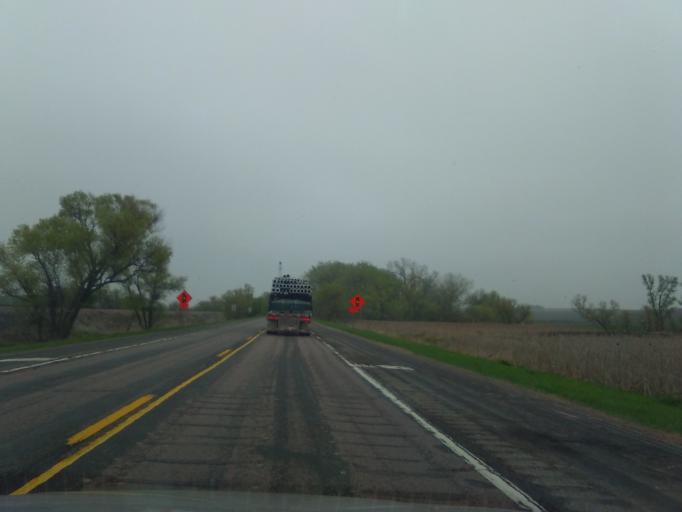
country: US
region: Nebraska
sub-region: Burt County
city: Oakland
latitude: 41.8057
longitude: -96.4791
